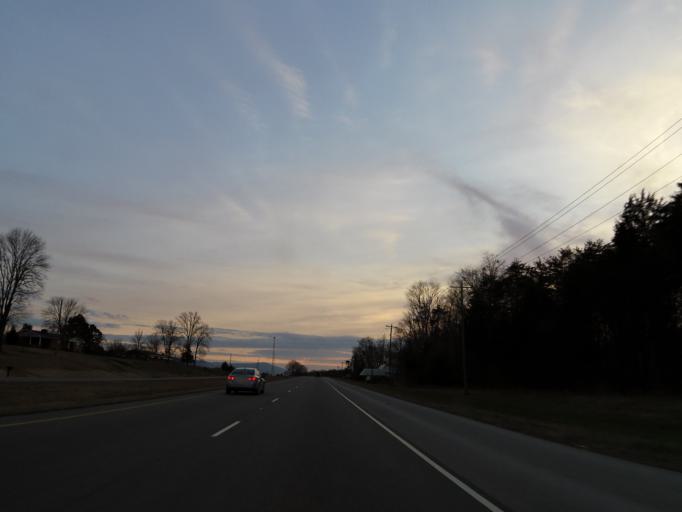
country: US
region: Tennessee
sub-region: McMinn County
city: Etowah
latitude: 35.3654
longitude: -84.5135
